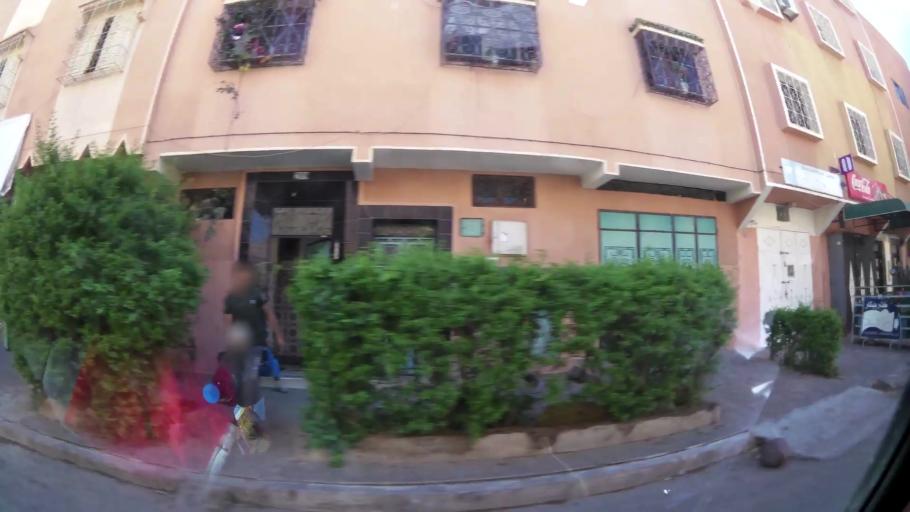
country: MA
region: Marrakech-Tensift-Al Haouz
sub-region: Marrakech
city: Marrakesh
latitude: 31.6600
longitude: -7.9879
